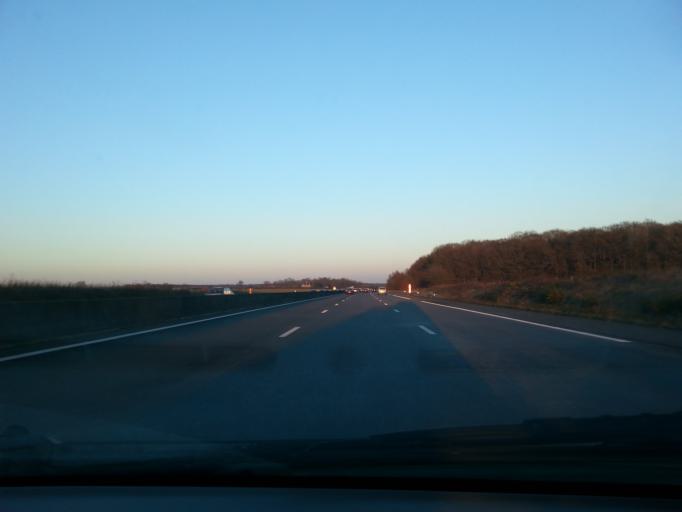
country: FR
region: Centre
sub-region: Departement d'Eure-et-Loir
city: Brou
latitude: 48.2548
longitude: 1.1283
